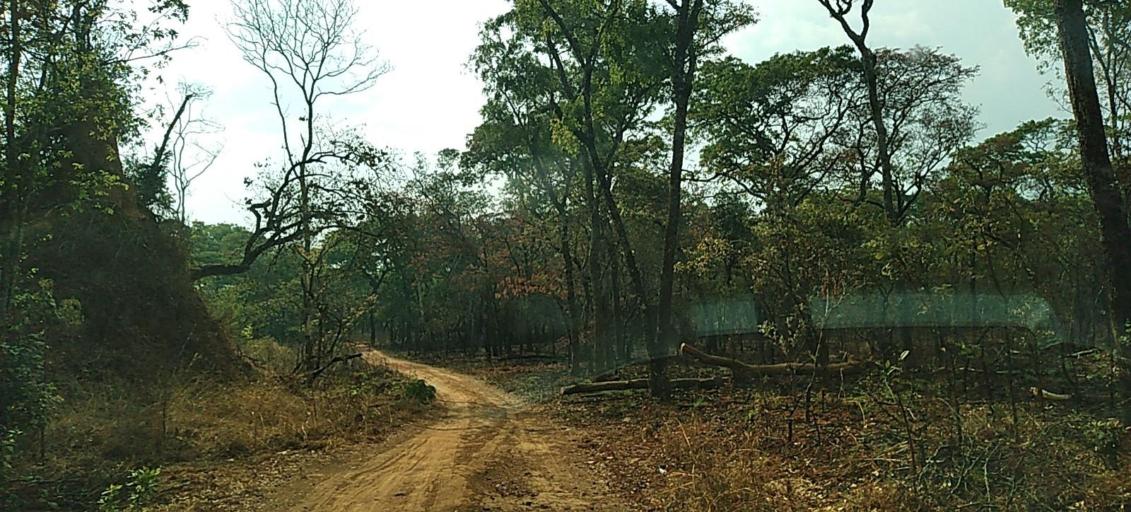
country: ZM
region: North-Western
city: Solwezi
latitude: -12.0691
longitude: 26.2230
